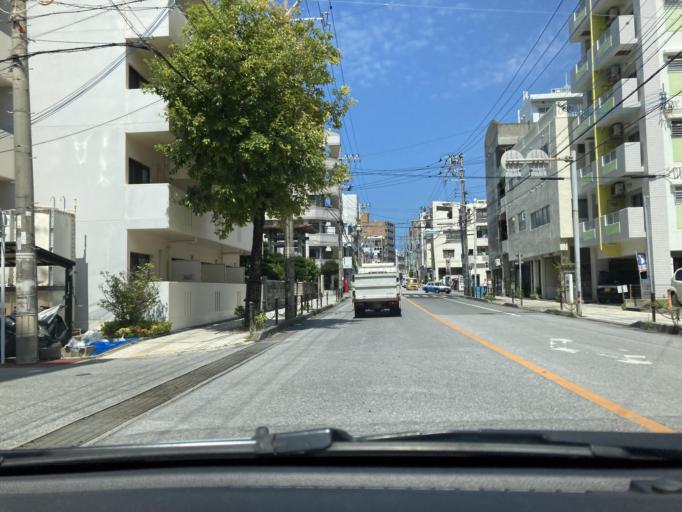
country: JP
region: Okinawa
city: Naha-shi
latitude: 26.2143
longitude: 127.6710
